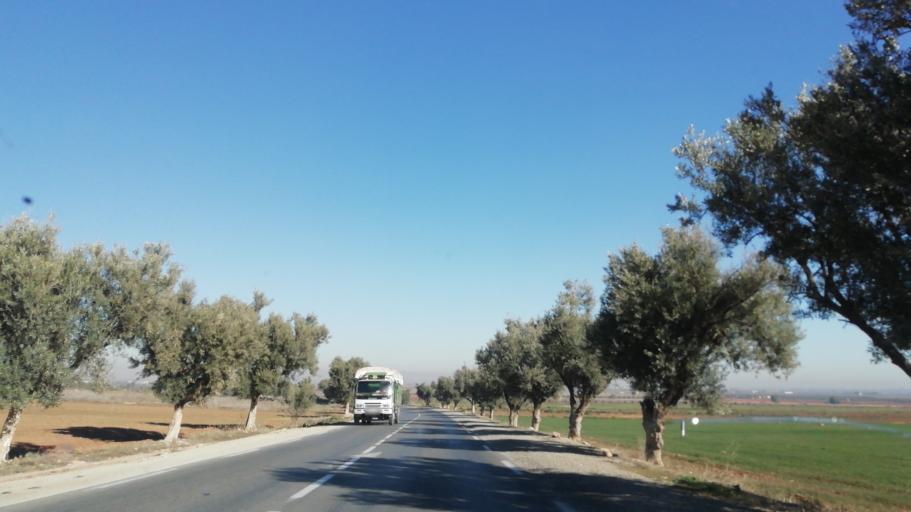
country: DZ
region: Mascara
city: Mascara
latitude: 35.2618
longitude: 0.1284
